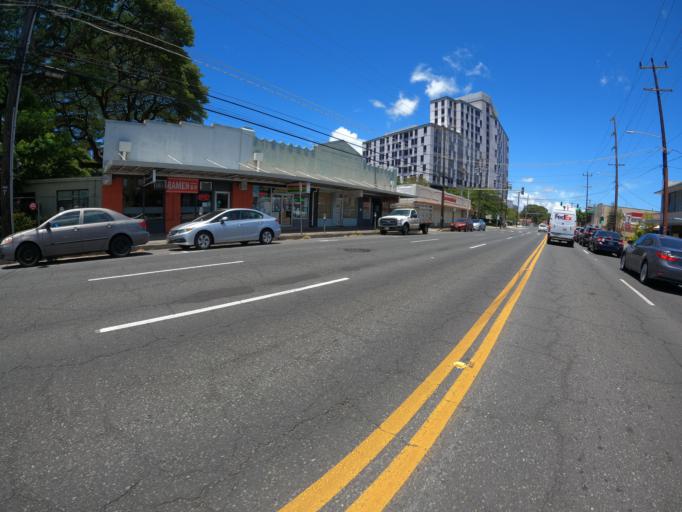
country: US
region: Hawaii
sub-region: Honolulu County
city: Honolulu
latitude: 21.2911
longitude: -157.8205
